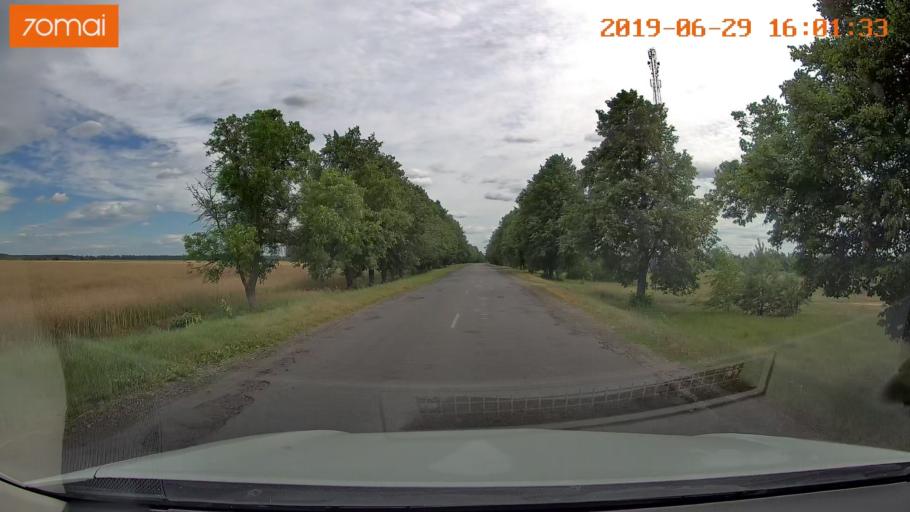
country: BY
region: Brest
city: Luninyets
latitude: 52.2457
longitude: 27.0165
